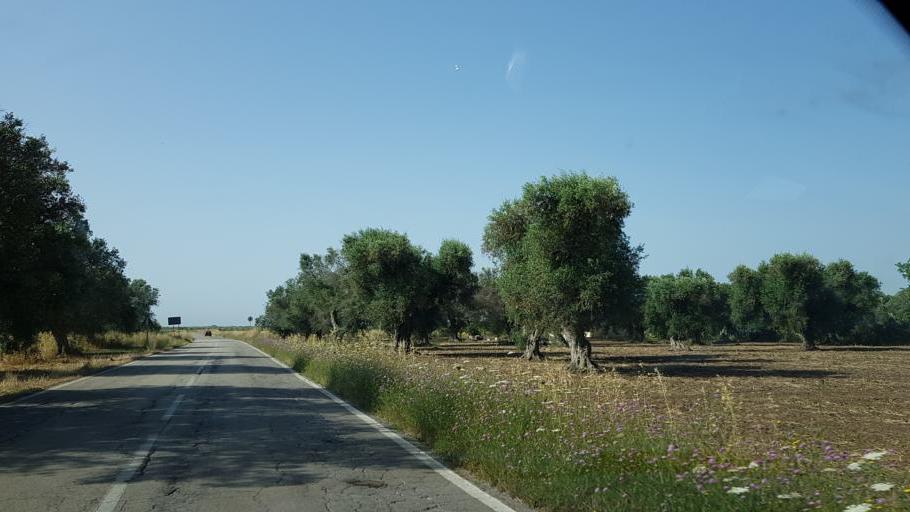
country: IT
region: Apulia
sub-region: Provincia di Brindisi
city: Mesagne
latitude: 40.5316
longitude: 17.8194
